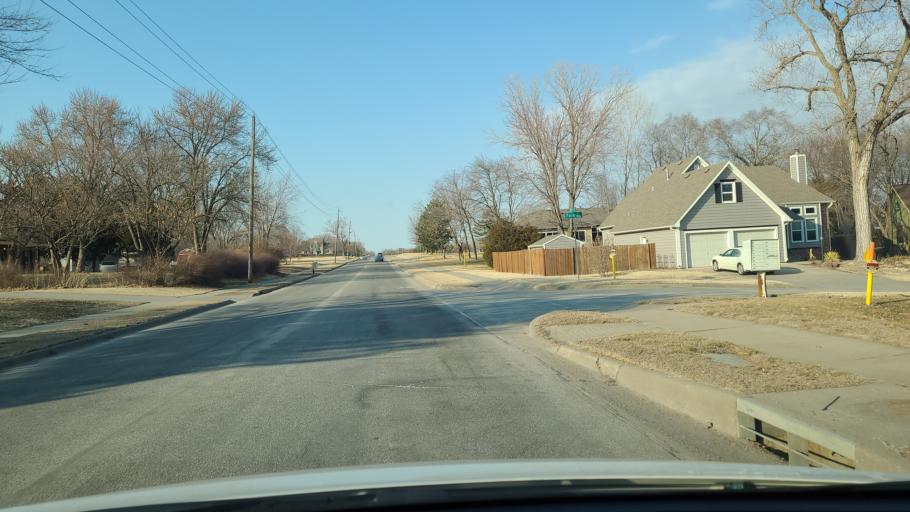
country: US
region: Kansas
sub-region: Douglas County
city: Lawrence
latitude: 38.9588
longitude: -95.2883
